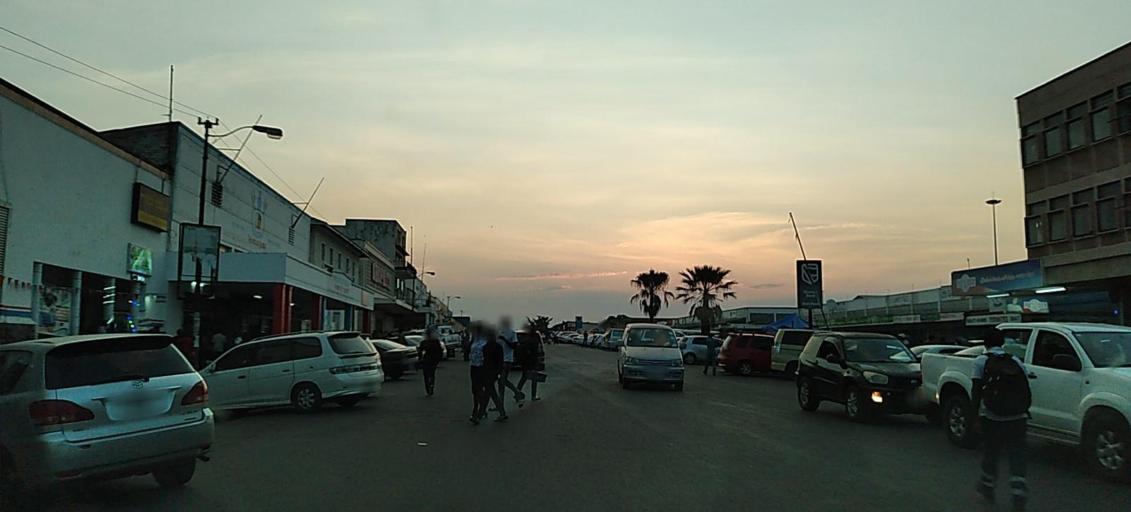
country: ZM
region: Copperbelt
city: Chingola
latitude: -12.5437
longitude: 27.8655
